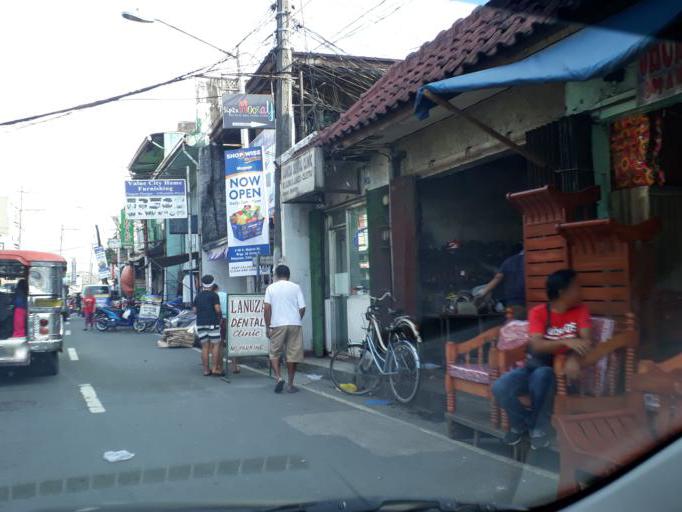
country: PH
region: Metro Manila
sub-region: Caloocan City
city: Niugan
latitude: 14.6440
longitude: 120.9748
